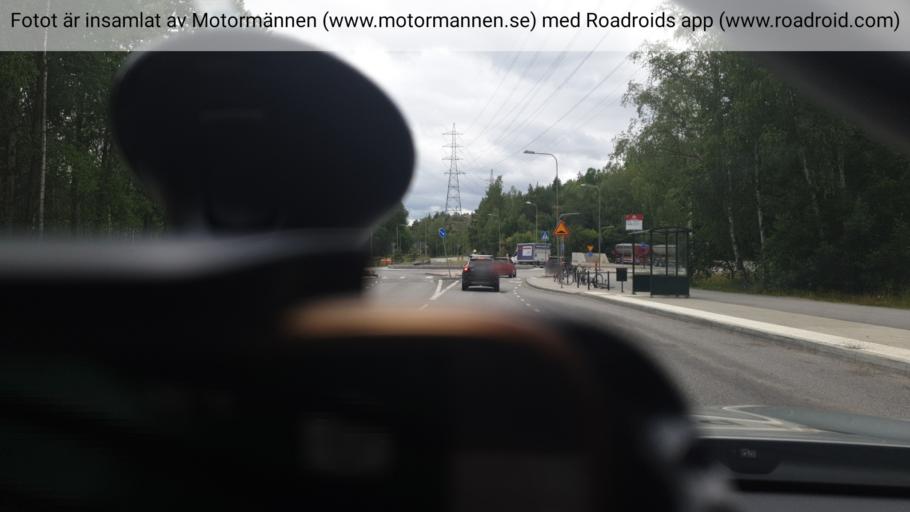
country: SE
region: Stockholm
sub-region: Huddinge Kommun
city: Huddinge
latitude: 59.2360
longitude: 18.0357
